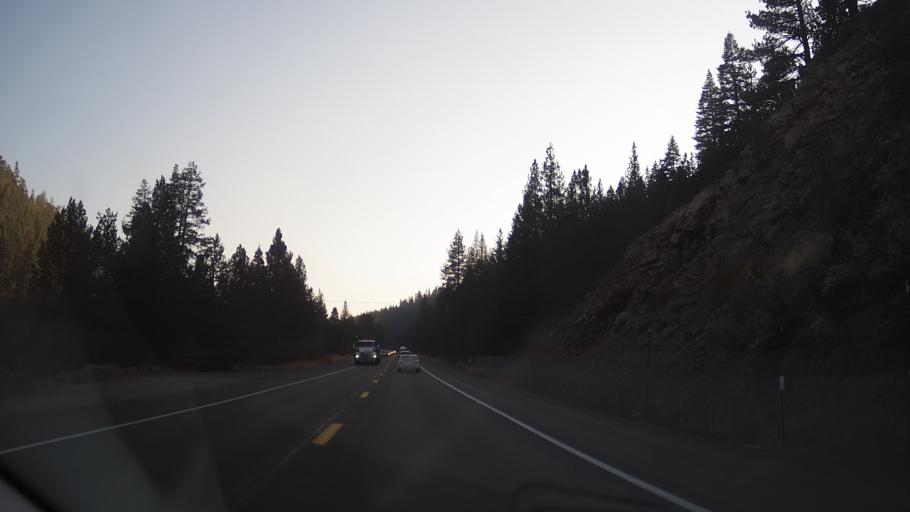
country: US
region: California
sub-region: Nevada County
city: Truckee
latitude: 39.2532
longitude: -120.2115
